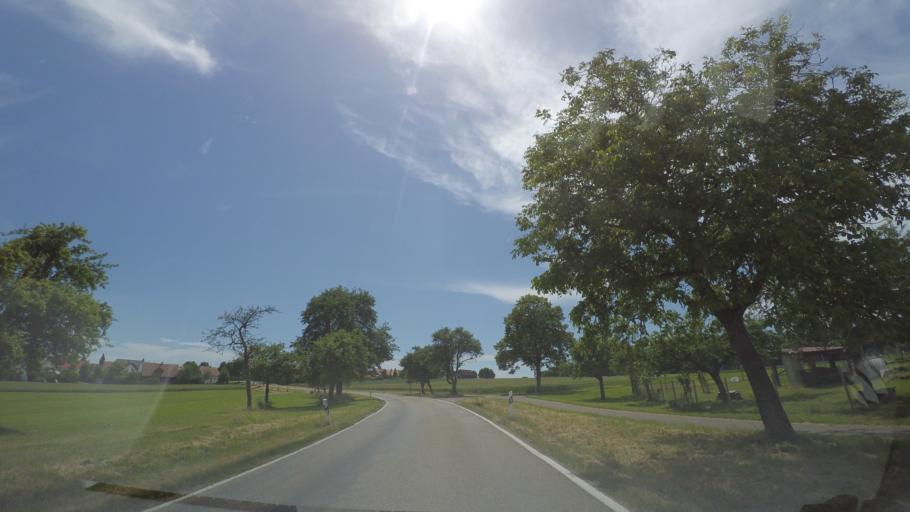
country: DE
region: Baden-Wuerttemberg
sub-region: Regierungsbezirk Stuttgart
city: Kaisersbach
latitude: 48.9351
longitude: 9.6397
